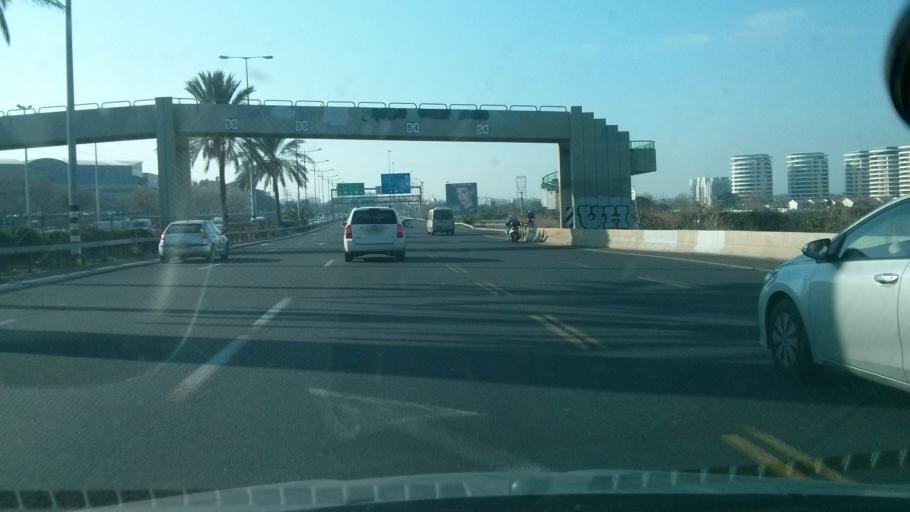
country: IL
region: Tel Aviv
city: Herzliya Pituah
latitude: 32.1477
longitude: 34.8035
